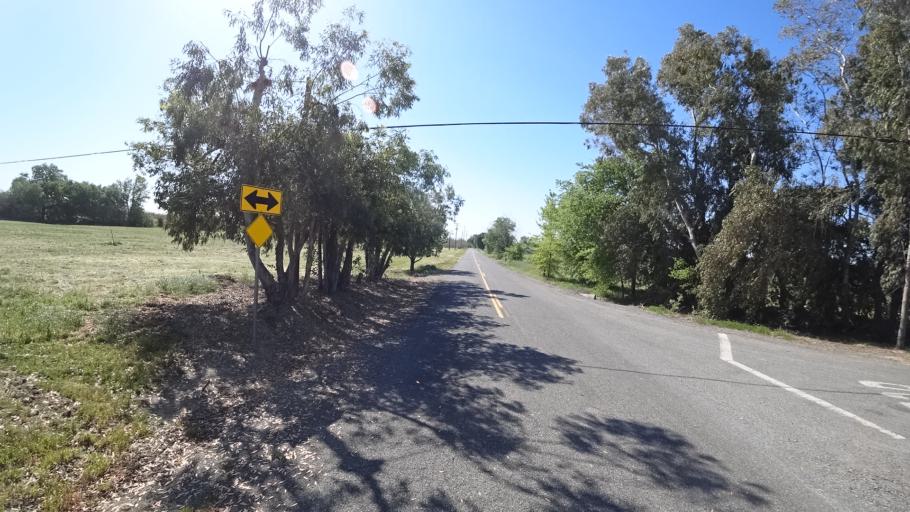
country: US
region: California
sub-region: Glenn County
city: Hamilton City
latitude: 39.7216
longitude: -122.0117
